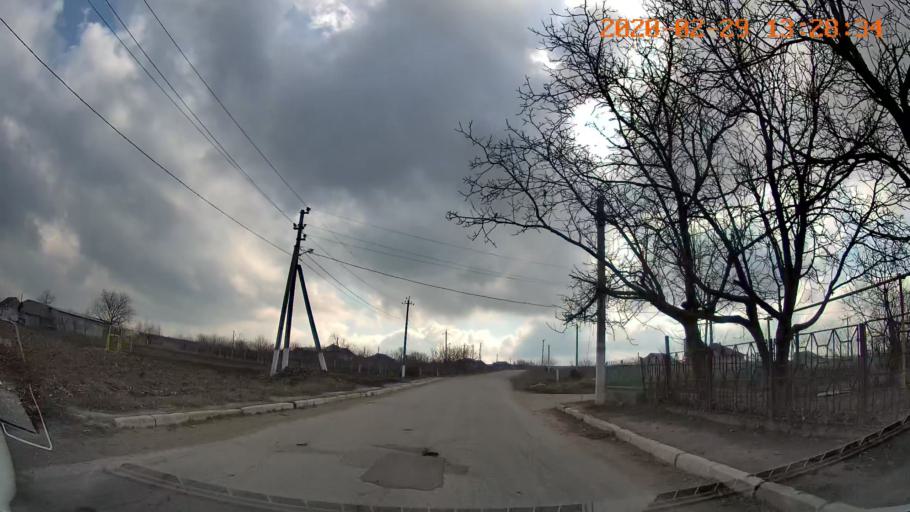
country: MD
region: Telenesti
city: Camenca
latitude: 47.9041
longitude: 28.6422
